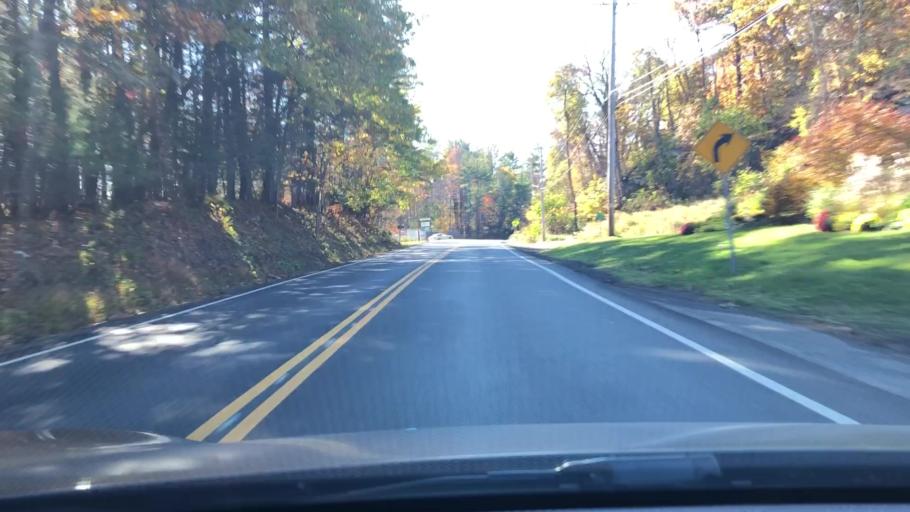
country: US
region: New York
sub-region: Ulster County
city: Zena
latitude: 42.0430
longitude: -74.0773
